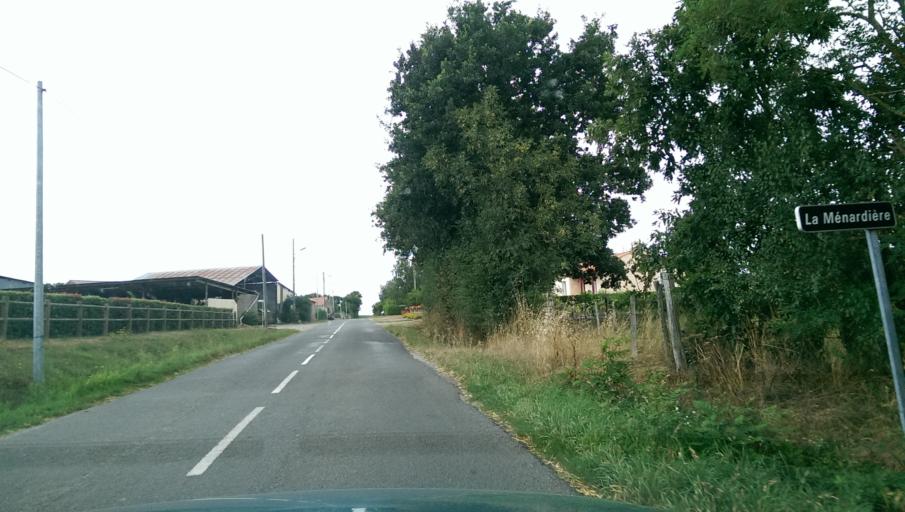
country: FR
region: Pays de la Loire
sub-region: Departement de la Loire-Atlantique
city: La Planche
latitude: 47.0043
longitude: -1.4091
